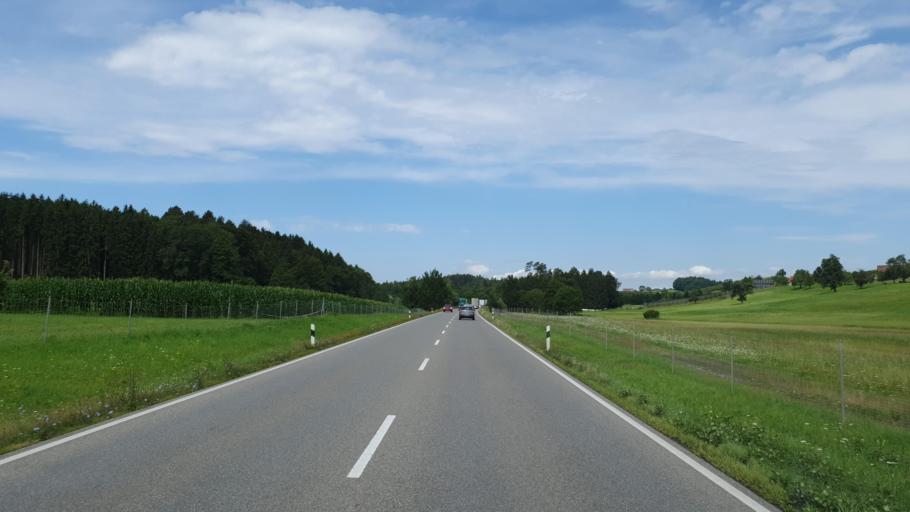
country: DE
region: Bavaria
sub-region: Swabia
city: Bodolz
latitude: 47.5862
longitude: 9.6556
